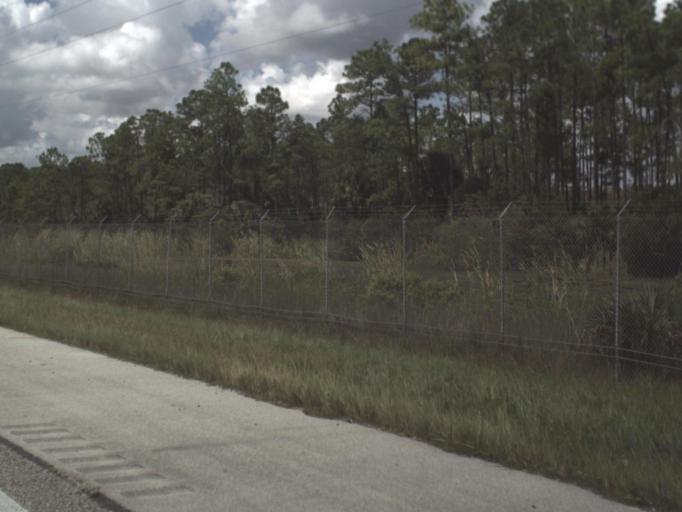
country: US
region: Florida
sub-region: Collier County
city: Immokalee
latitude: 26.1702
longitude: -81.0018
